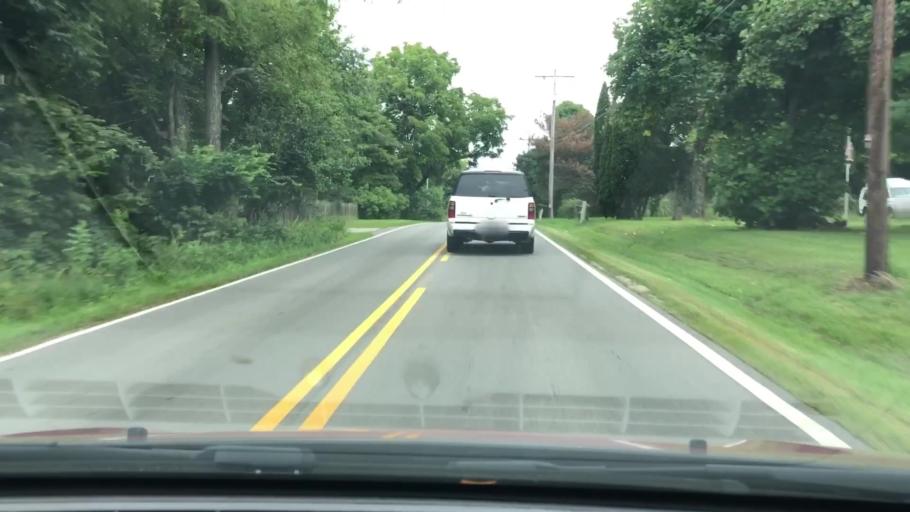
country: US
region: Ohio
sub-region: Franklin County
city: New Albany
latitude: 40.1346
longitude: -82.8417
